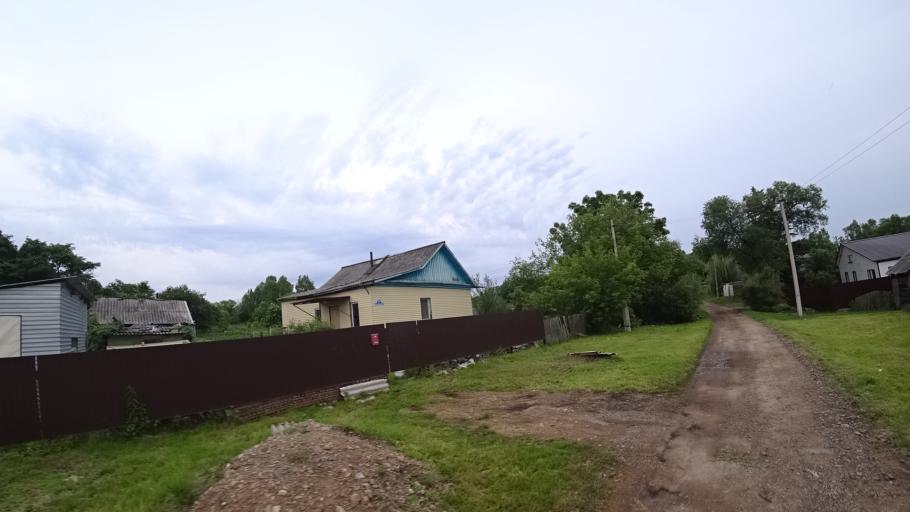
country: RU
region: Primorskiy
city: Novosysoyevka
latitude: 44.2235
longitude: 133.3540
